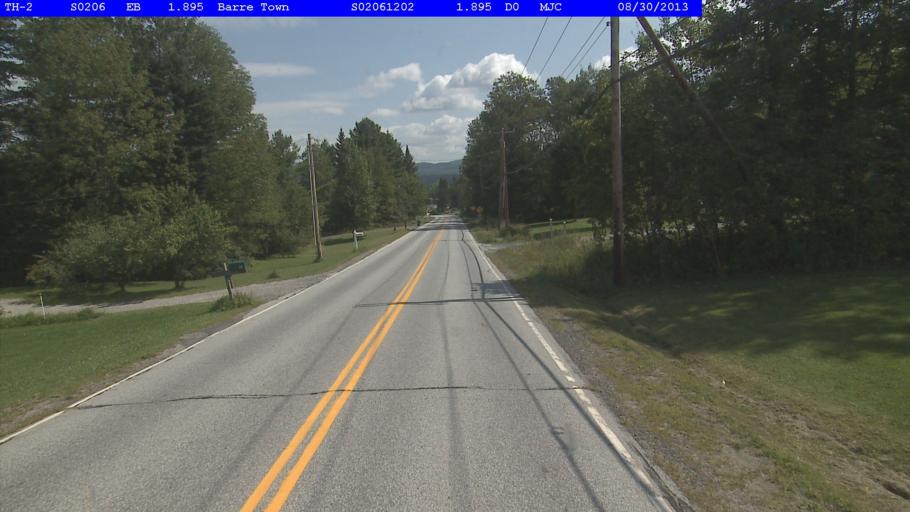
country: US
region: Vermont
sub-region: Washington County
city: South Barre
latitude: 44.1597
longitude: -72.4597
